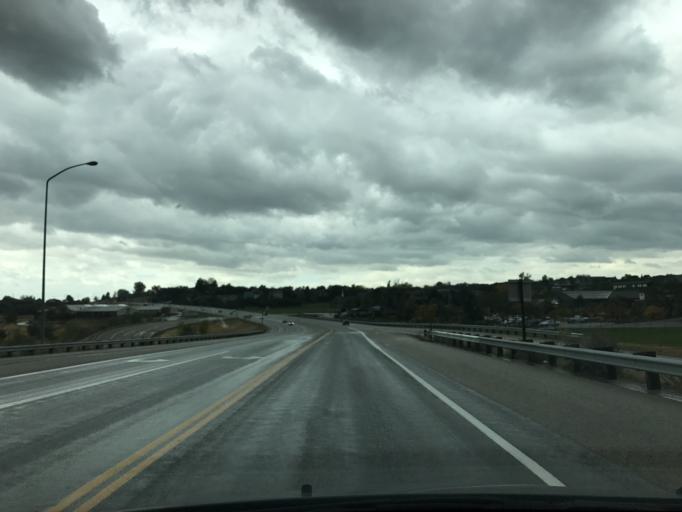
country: US
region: Utah
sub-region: Davis County
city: South Weber
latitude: 41.1079
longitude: -111.9113
